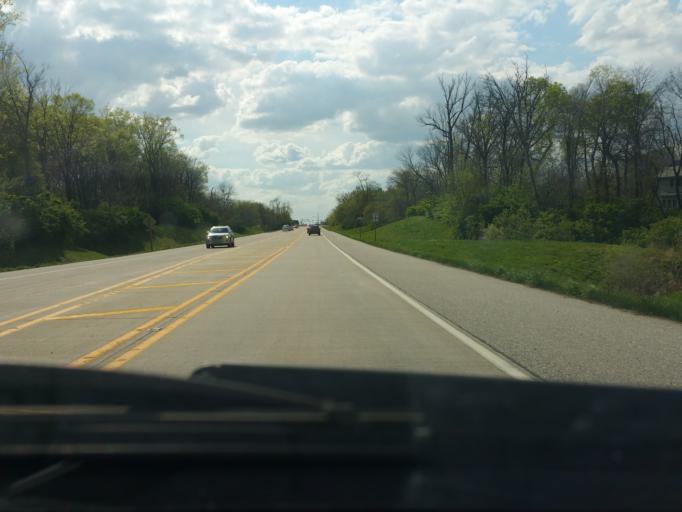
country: US
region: Illinois
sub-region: Madison County
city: Edwardsville
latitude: 38.7873
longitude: -89.9407
